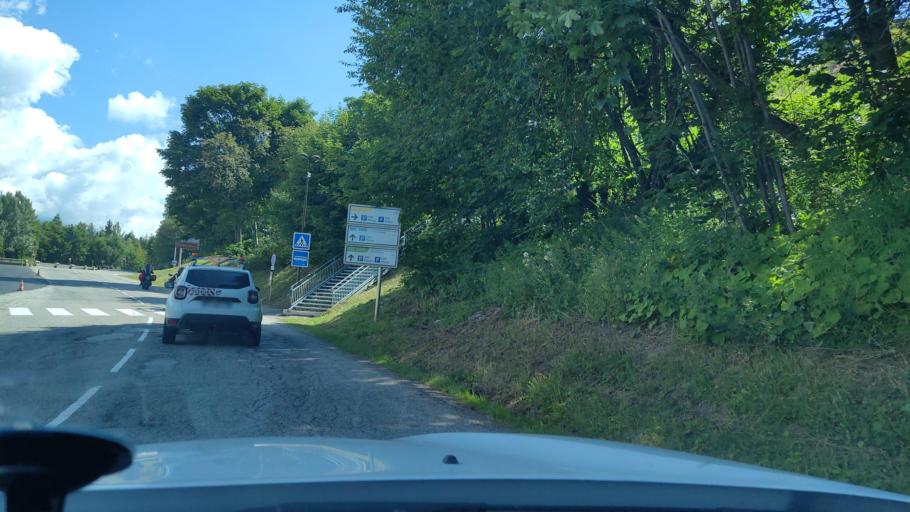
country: FR
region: Rhone-Alpes
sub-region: Departement de la Savoie
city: Seez
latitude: 45.5956
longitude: 6.7913
